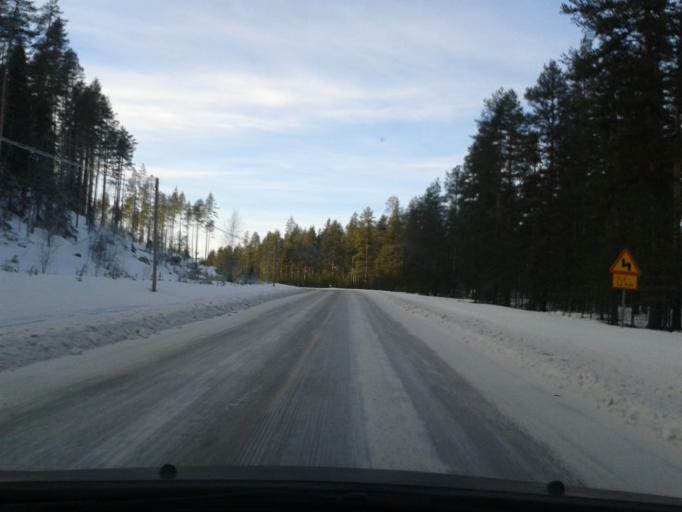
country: SE
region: Vaesternorrland
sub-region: OErnskoeldsviks Kommun
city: Bredbyn
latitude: 63.6743
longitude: 17.8174
